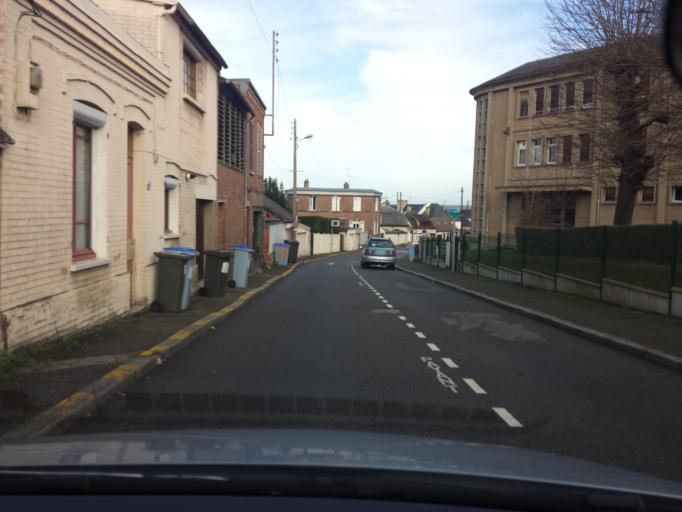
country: FR
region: Haute-Normandie
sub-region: Departement de l'Eure
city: Evreux
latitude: 49.0200
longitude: 1.1524
